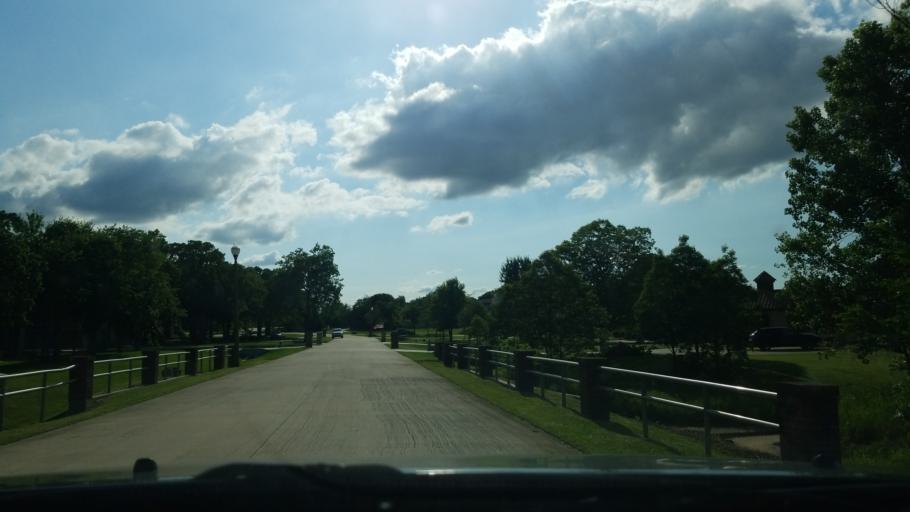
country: US
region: Texas
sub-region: Denton County
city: Denton
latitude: 33.1725
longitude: -97.1390
